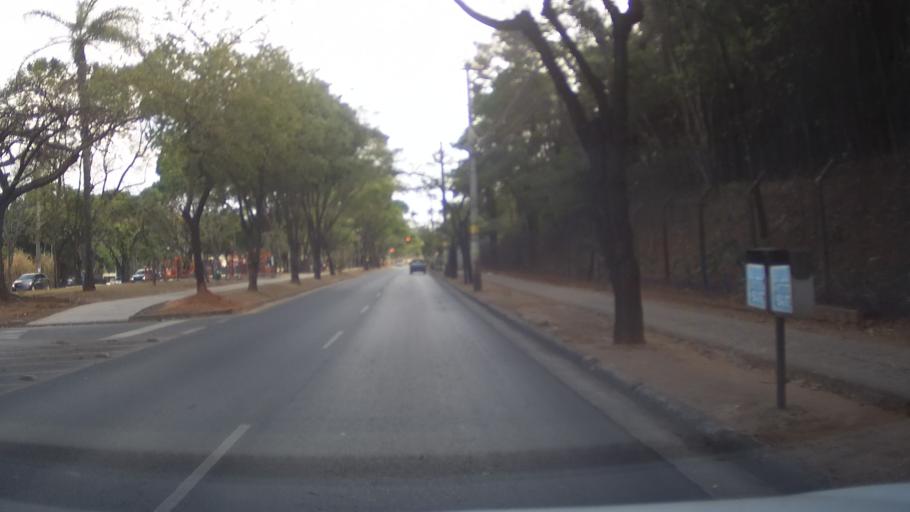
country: BR
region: Minas Gerais
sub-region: Belo Horizonte
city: Belo Horizonte
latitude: -19.8862
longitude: -43.9180
